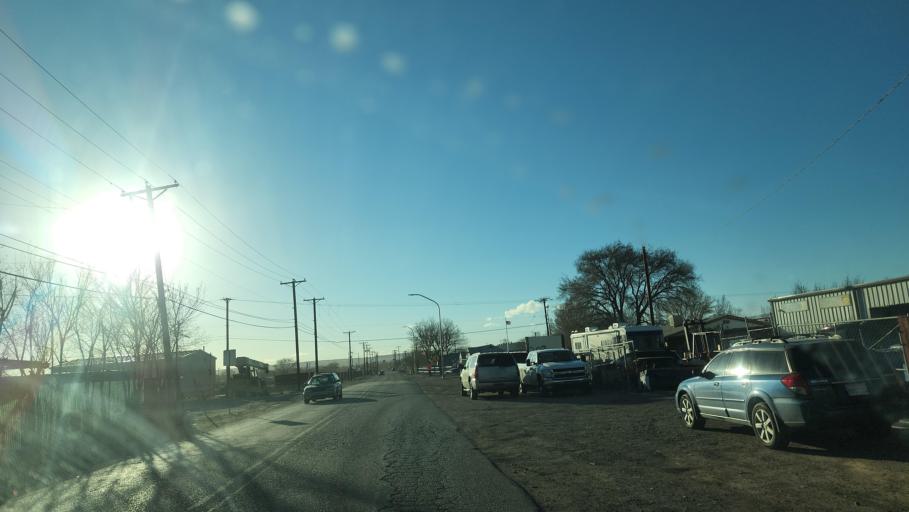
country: US
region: New Mexico
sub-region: Bernalillo County
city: South Valley
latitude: 35.0150
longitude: -106.6564
